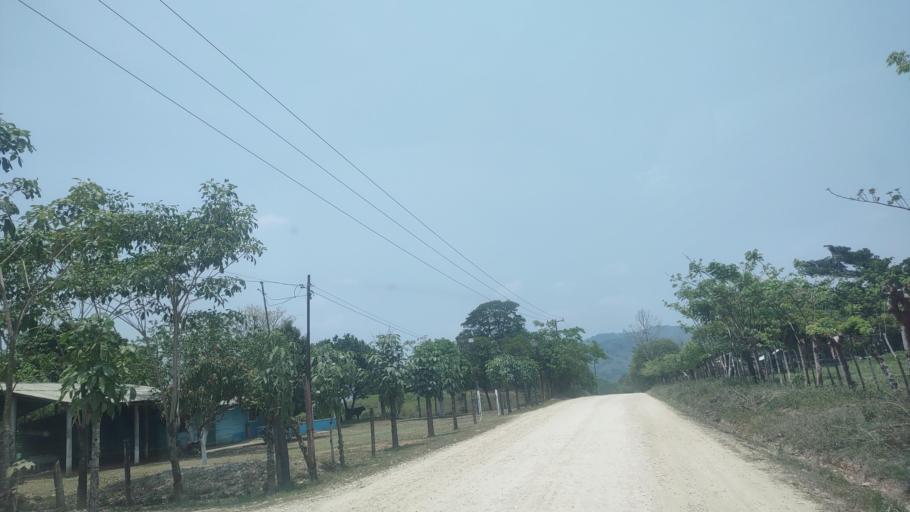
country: MX
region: Chiapas
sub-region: Tecpatan
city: Raudales Malpaso
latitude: 17.4601
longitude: -93.8053
